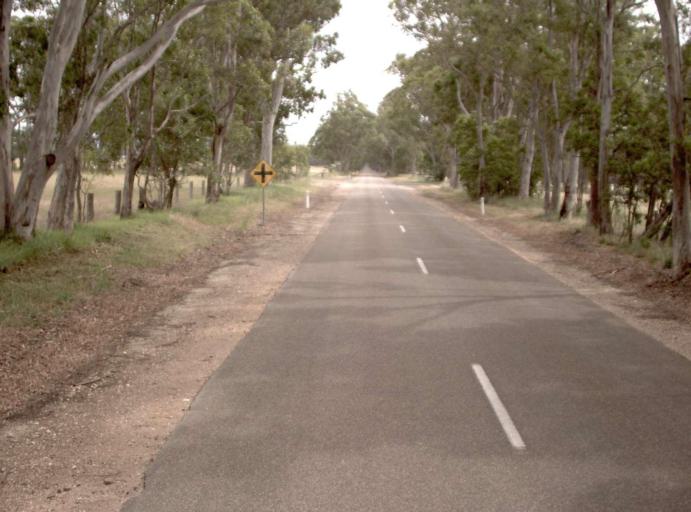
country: AU
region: Victoria
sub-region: Wellington
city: Sale
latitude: -37.8707
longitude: 147.0672
